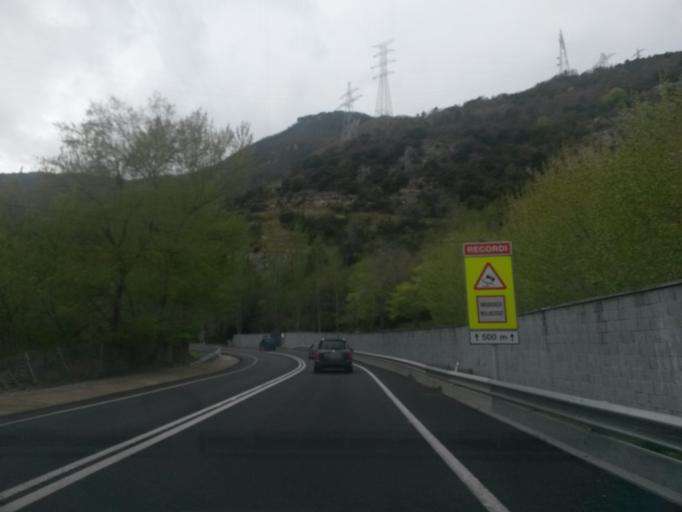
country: ES
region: Catalonia
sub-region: Provincia de Barcelona
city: Vallcebre
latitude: 42.1712
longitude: 1.8594
